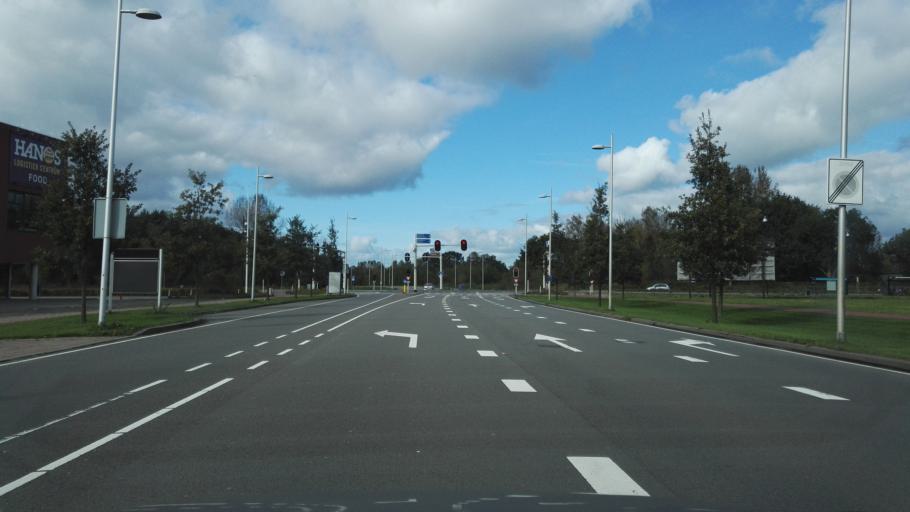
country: NL
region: Gelderland
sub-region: Gemeente Apeldoorn
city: Apeldoorn
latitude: 52.2452
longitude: 5.9899
